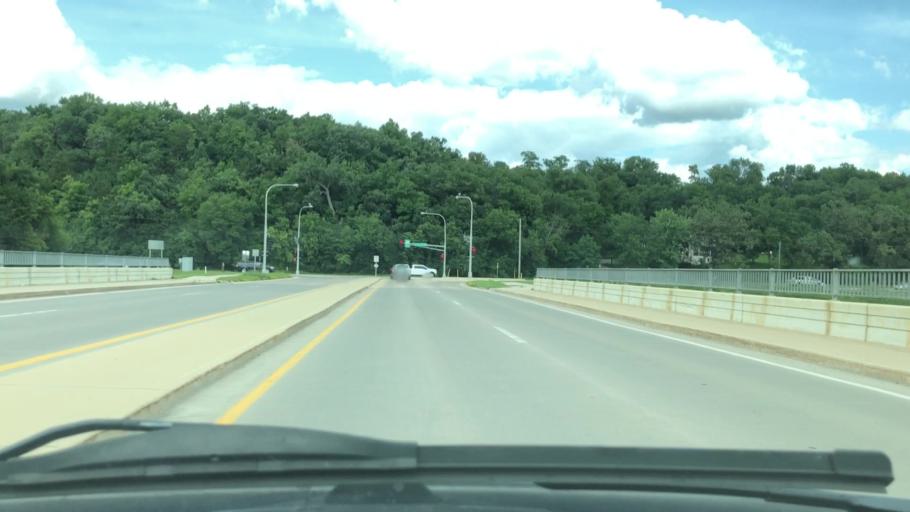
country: US
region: Minnesota
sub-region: Olmsted County
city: Rochester
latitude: 43.9974
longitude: -92.4980
